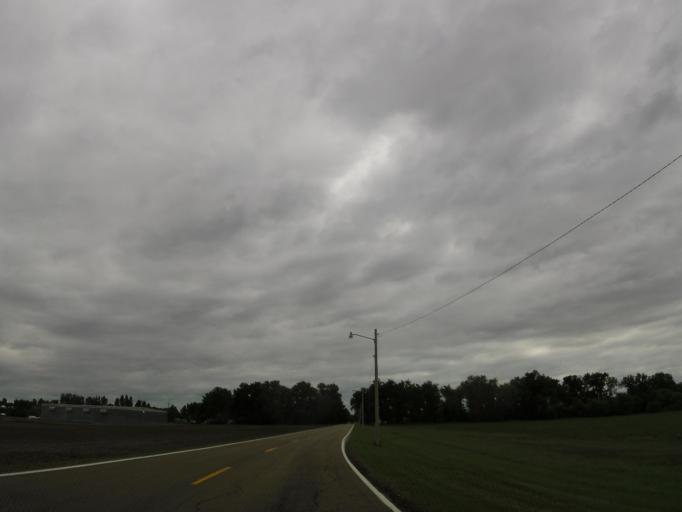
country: US
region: North Dakota
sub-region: Walsh County
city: Grafton
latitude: 48.6267
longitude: -97.4490
